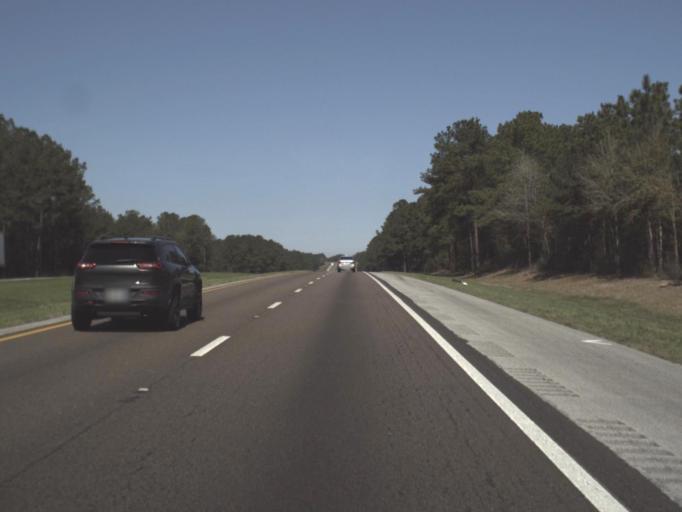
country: US
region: Florida
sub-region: Walton County
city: DeFuniak Springs
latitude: 30.7093
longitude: -86.1669
